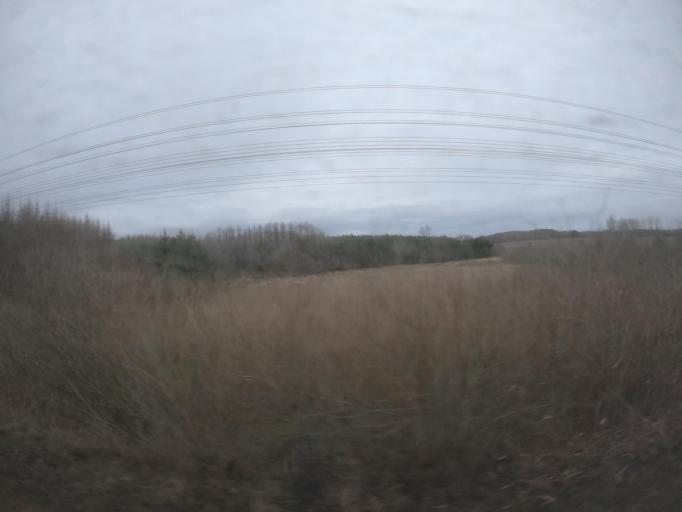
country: PL
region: West Pomeranian Voivodeship
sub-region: Powiat szczecinecki
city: Borne Sulinowo
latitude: 53.6578
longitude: 16.5687
